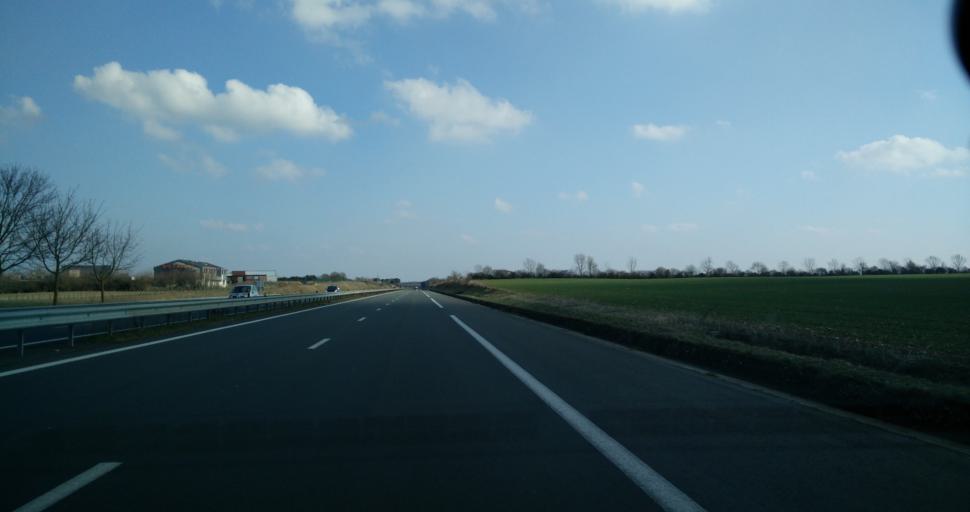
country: FR
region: Poitou-Charentes
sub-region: Departement de la Charente-Maritime
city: Saint-Jean-de-Liversay
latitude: 46.2263
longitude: -0.8735
